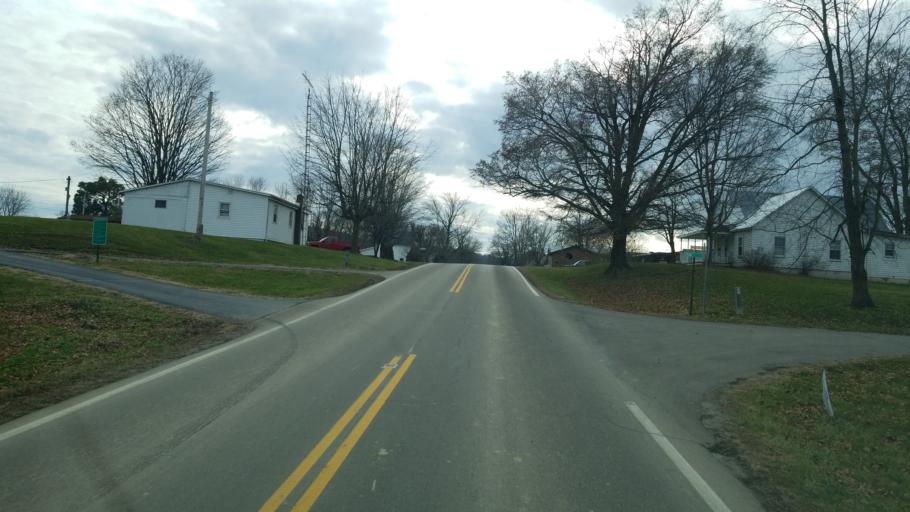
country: US
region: Ohio
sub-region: Highland County
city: Greenfield
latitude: 39.1755
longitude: -83.3475
